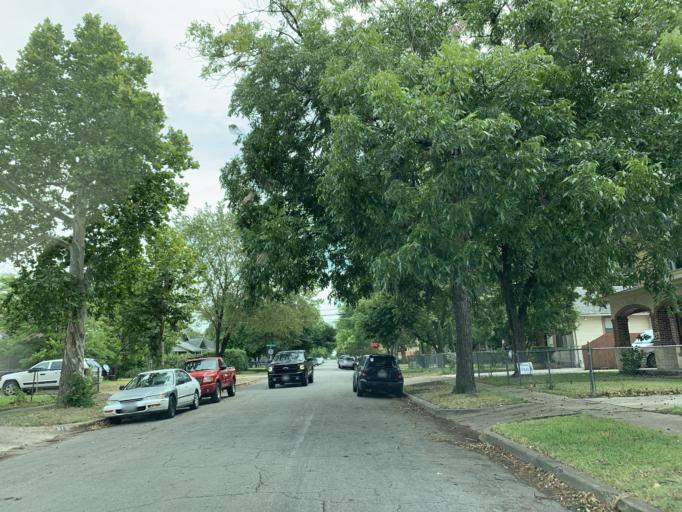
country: US
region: Texas
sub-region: Dallas County
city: Cockrell Hill
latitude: 32.7437
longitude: -96.8503
